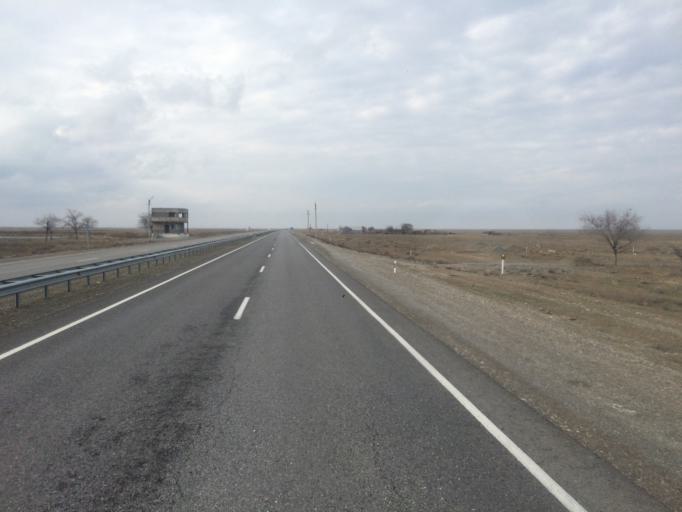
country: KZ
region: Ongtustik Qazaqstan
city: Turkestan
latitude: 43.5258
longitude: 67.7937
